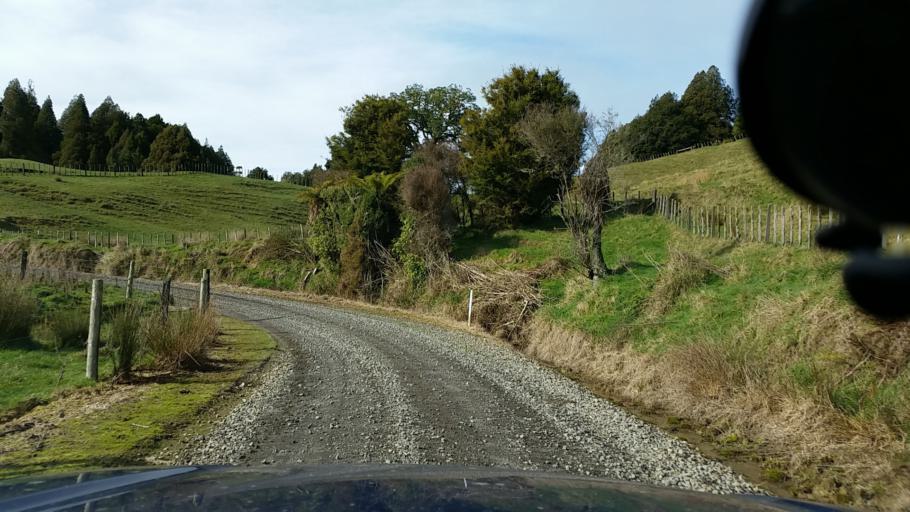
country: NZ
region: Taranaki
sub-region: New Plymouth District
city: Waitara
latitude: -39.0338
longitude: 174.7731
